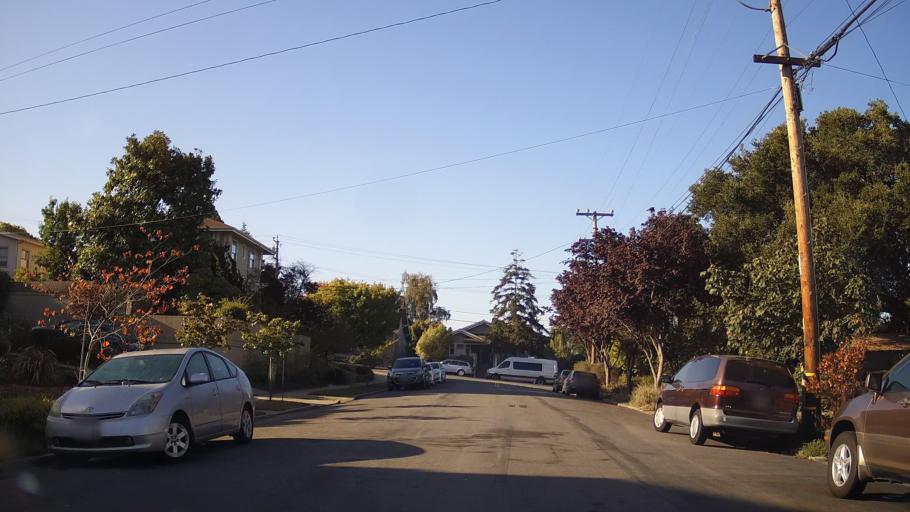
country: US
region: California
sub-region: Alameda County
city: Albany
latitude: 37.8877
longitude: -122.2831
